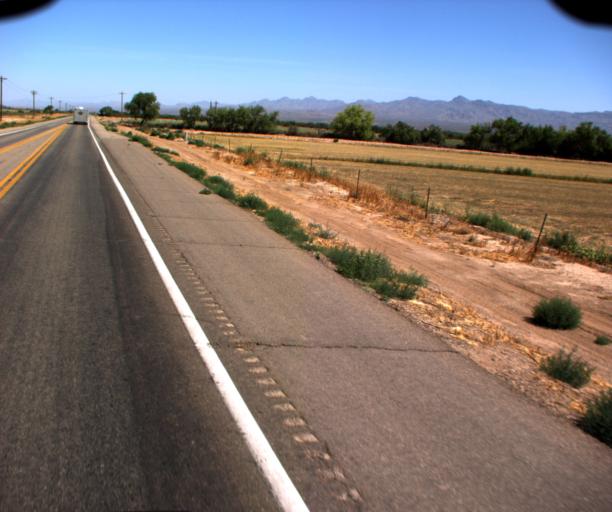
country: US
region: Arizona
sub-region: Graham County
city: Pima
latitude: 32.9630
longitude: -109.9209
